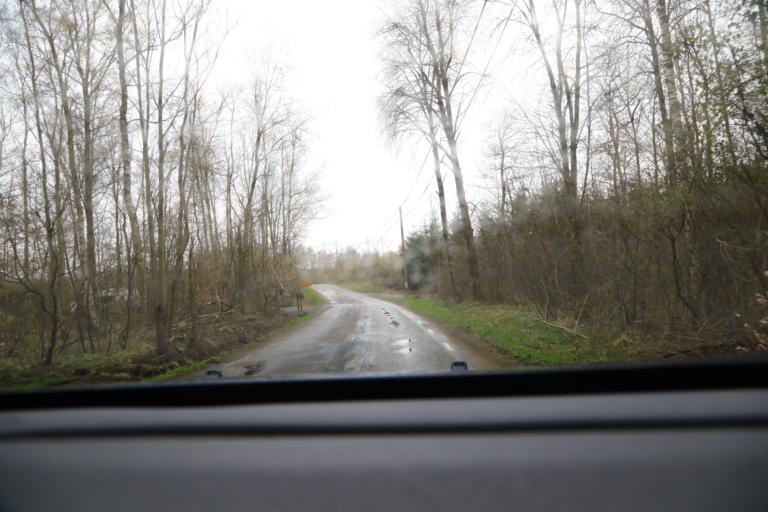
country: SE
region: Halland
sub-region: Kungsbacka Kommun
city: Frillesas
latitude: 57.2848
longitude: 12.2084
